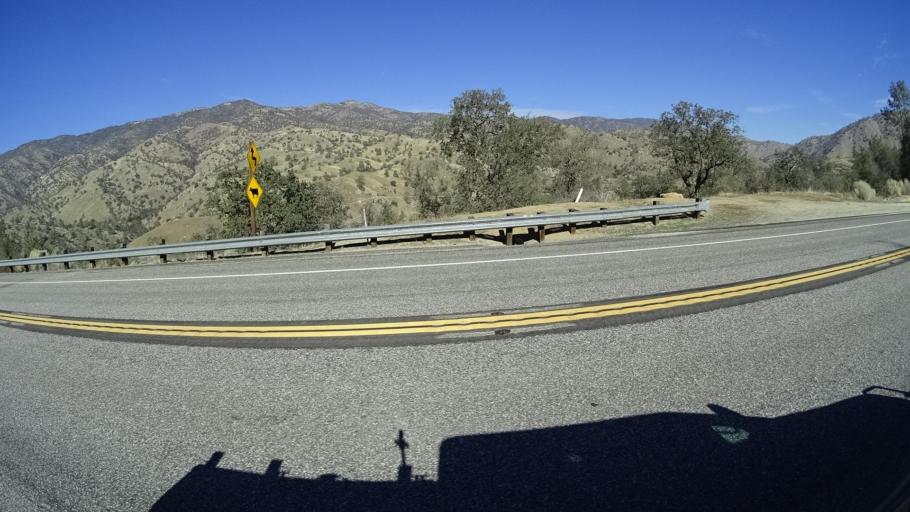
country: US
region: California
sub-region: Kern County
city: Bodfish
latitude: 35.5309
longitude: -118.6386
